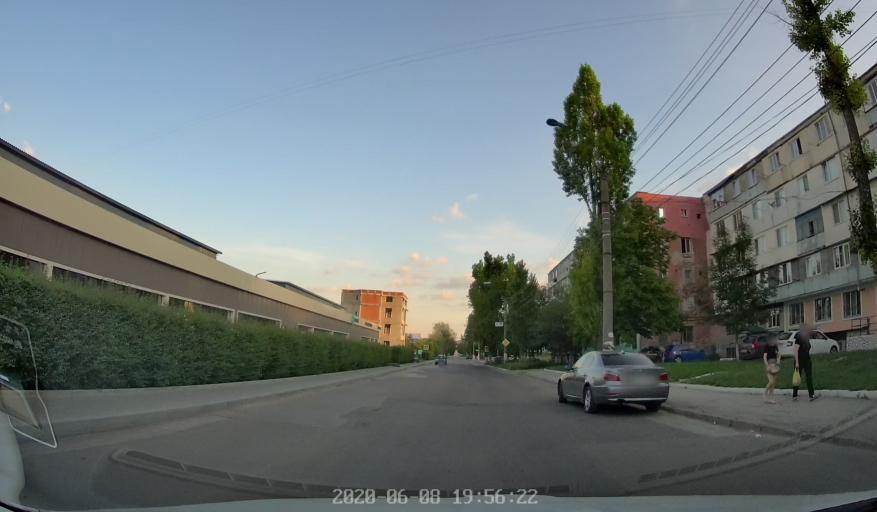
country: MD
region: Chisinau
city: Chisinau
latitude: 47.0228
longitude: 28.8832
